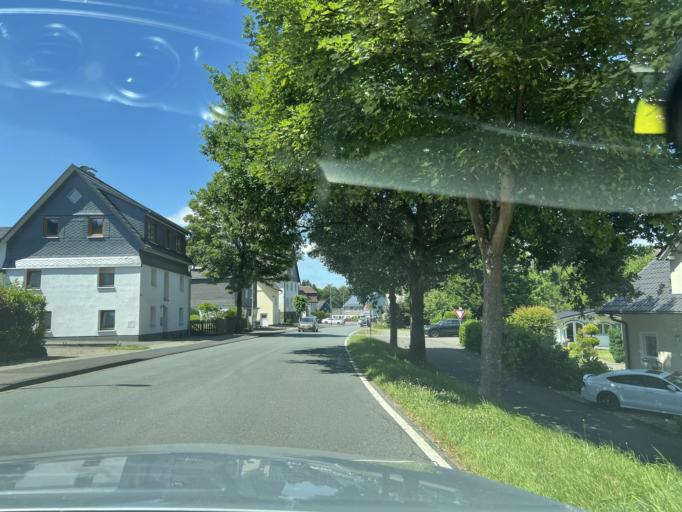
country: DE
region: North Rhine-Westphalia
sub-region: Regierungsbezirk Arnsberg
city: Wenden
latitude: 50.9729
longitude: 7.8575
